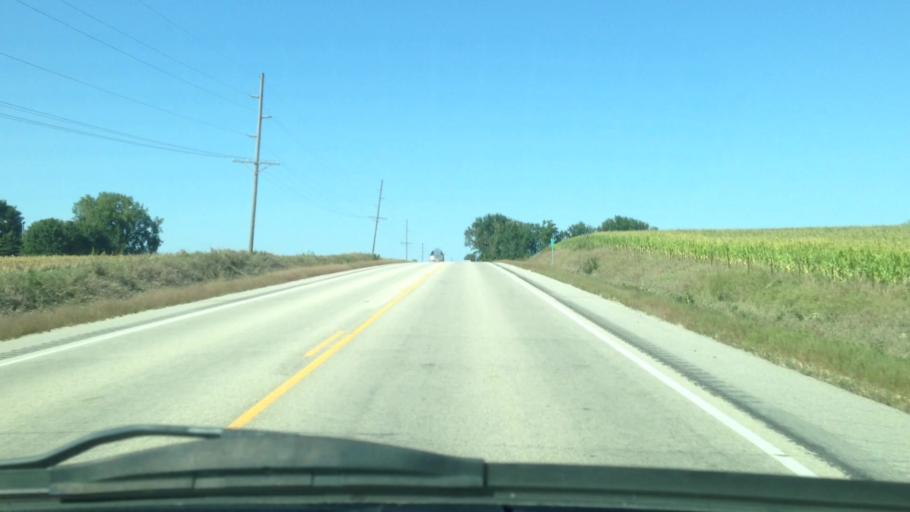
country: US
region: Minnesota
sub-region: Fillmore County
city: Rushford
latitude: 43.9056
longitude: -91.7401
